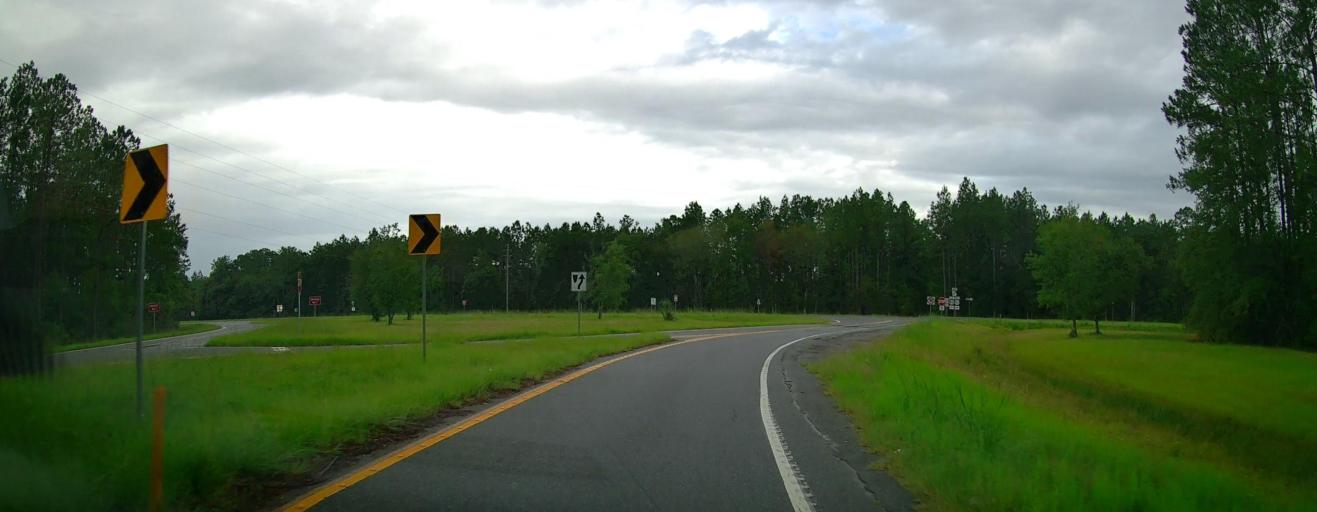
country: US
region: Georgia
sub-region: Ware County
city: Deenwood
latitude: 31.2634
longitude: -82.5180
